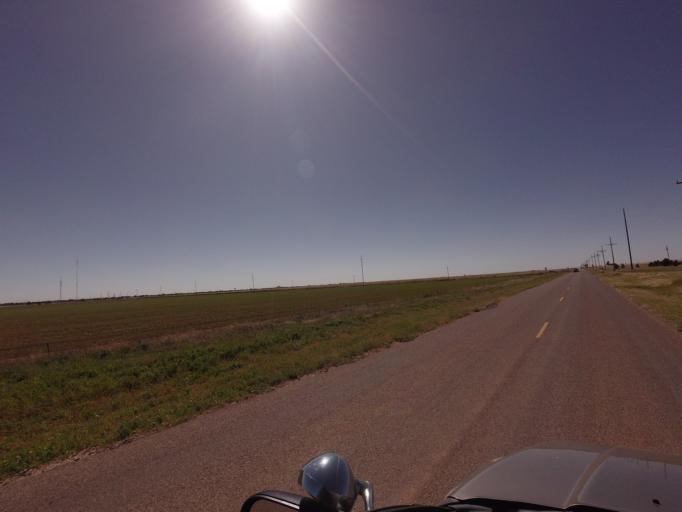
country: US
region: New Mexico
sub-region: Curry County
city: Clovis
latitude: 34.4484
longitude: -103.2118
